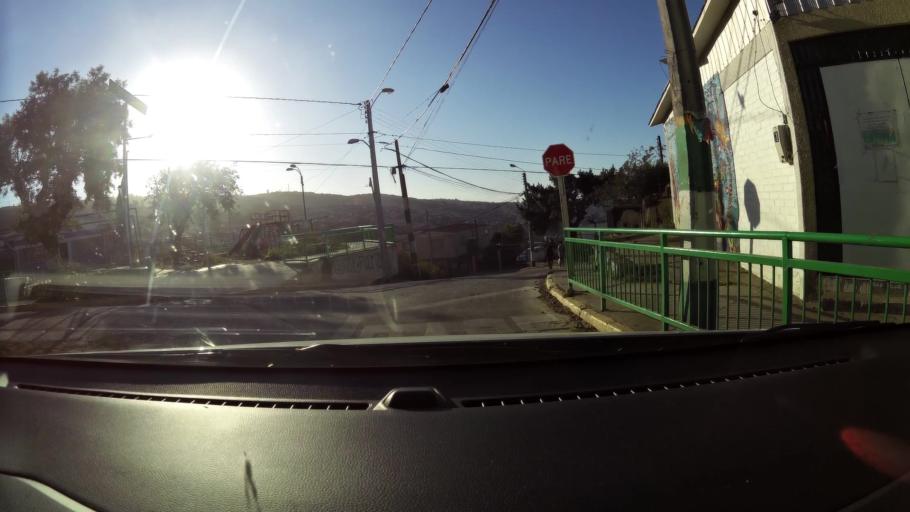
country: CL
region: Valparaiso
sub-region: Provincia de Valparaiso
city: Valparaiso
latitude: -33.0585
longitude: -71.6148
